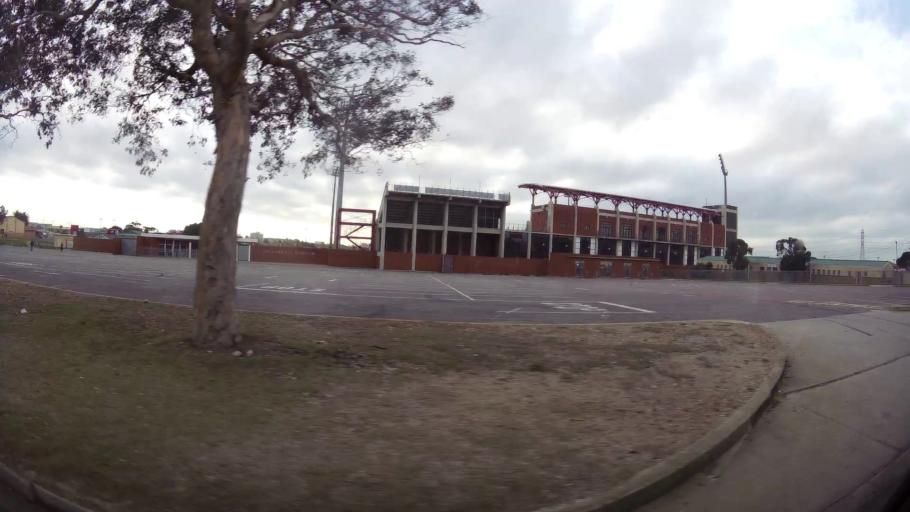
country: ZA
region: Eastern Cape
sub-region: Nelson Mandela Bay Metropolitan Municipality
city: Port Elizabeth
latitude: -33.9148
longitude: 25.5585
